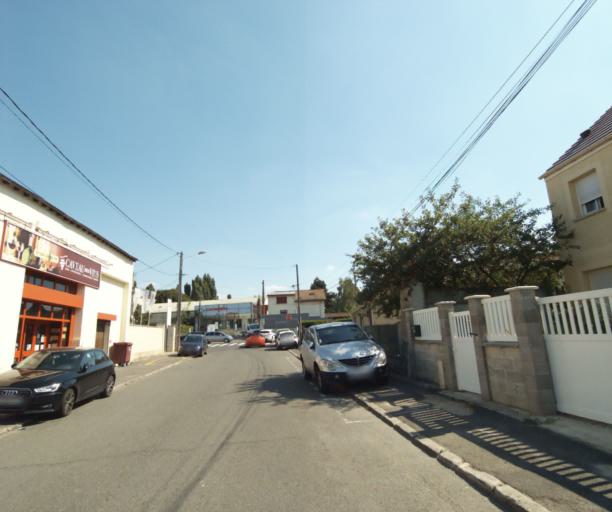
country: FR
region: Ile-de-France
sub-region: Departement de Seine-et-Marne
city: Pomponne
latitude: 48.8752
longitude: 2.6931
